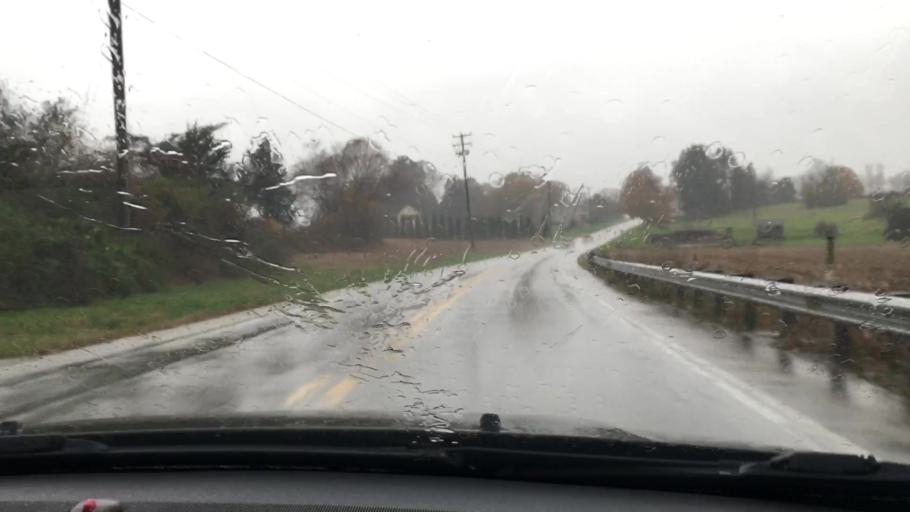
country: US
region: Pennsylvania
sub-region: York County
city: Stewartstown
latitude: 39.7602
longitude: -76.6258
